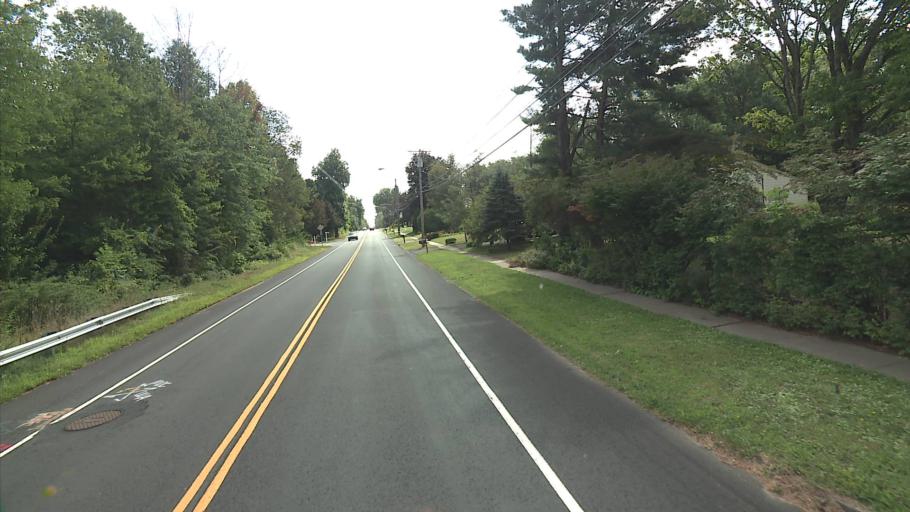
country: US
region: Connecticut
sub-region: Hartford County
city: West Hartford
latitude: 41.8023
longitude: -72.7391
